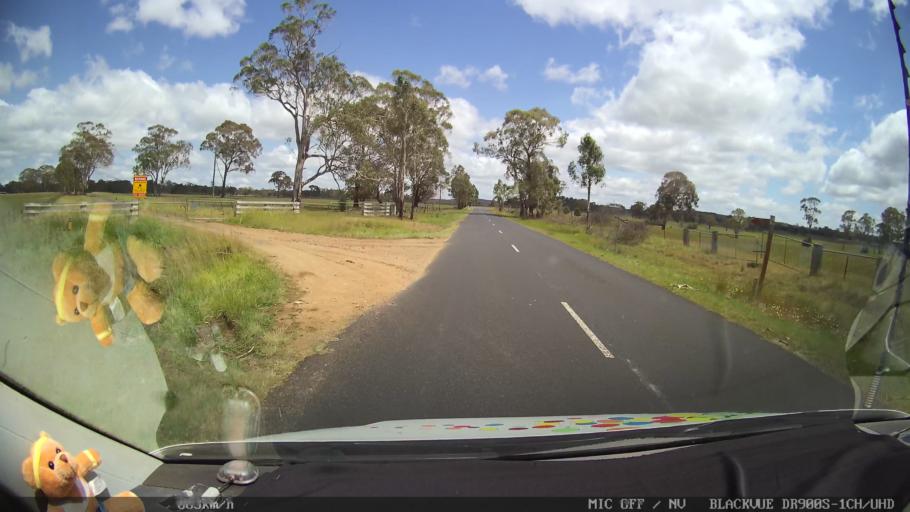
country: AU
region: New South Wales
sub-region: Glen Innes Severn
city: Glen Innes
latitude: -29.6217
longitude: 151.6695
